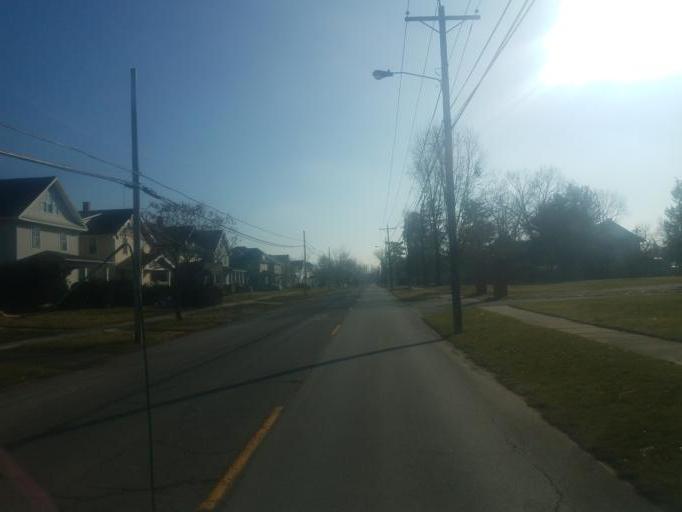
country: US
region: Ohio
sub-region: Seneca County
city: Tiffin
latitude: 41.1046
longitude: -83.1707
